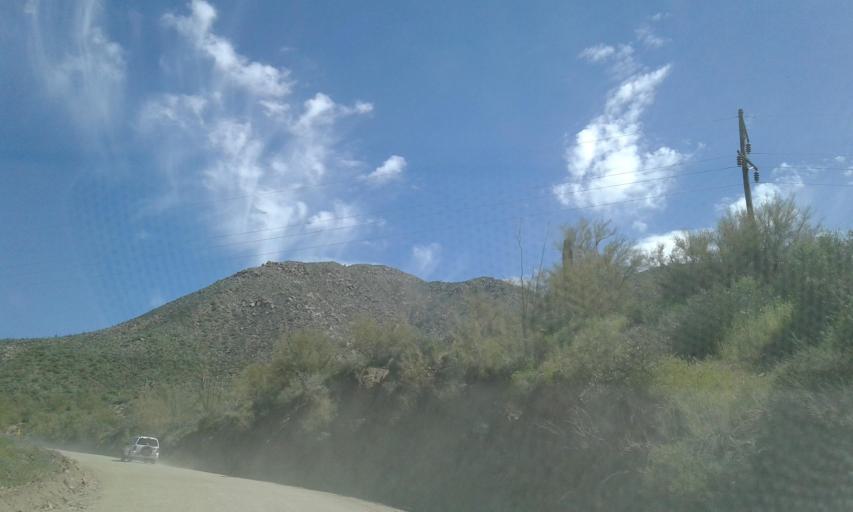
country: US
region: Arizona
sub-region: Gila County
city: Tonto Basin
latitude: 33.6021
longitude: -111.2025
